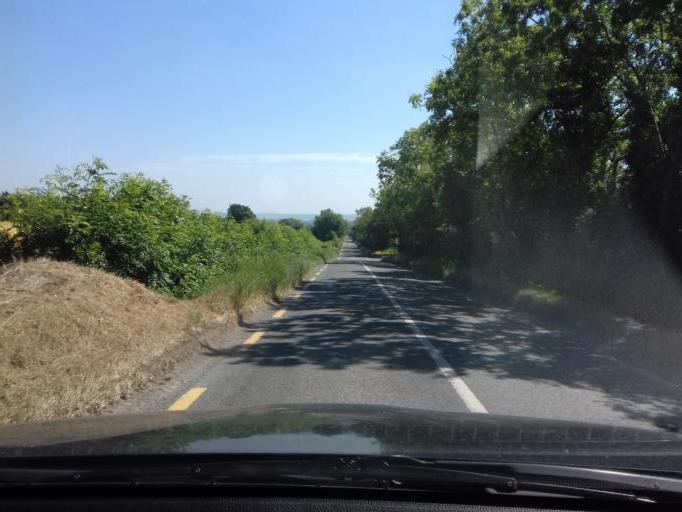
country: IE
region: Leinster
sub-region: An Mhi
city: Stamullin
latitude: 53.5580
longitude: -6.2724
